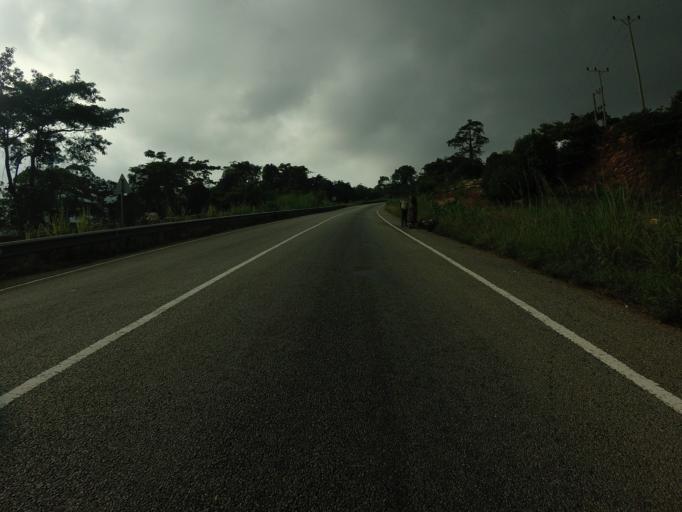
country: GH
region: Volta
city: Ho
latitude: 6.8117
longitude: 0.4207
